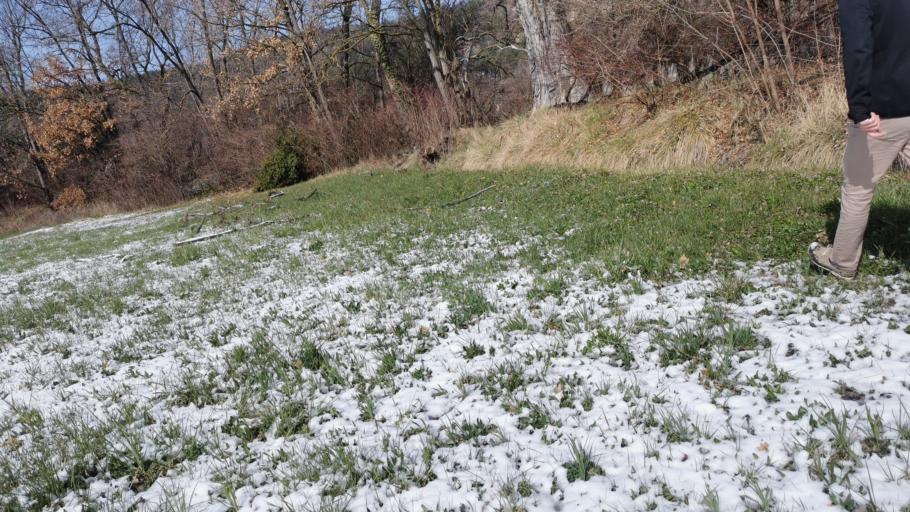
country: FR
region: Provence-Alpes-Cote d'Azur
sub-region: Departement des Alpes-de-Haute-Provence
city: Mallemoisson
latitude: 44.0582
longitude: 6.1671
